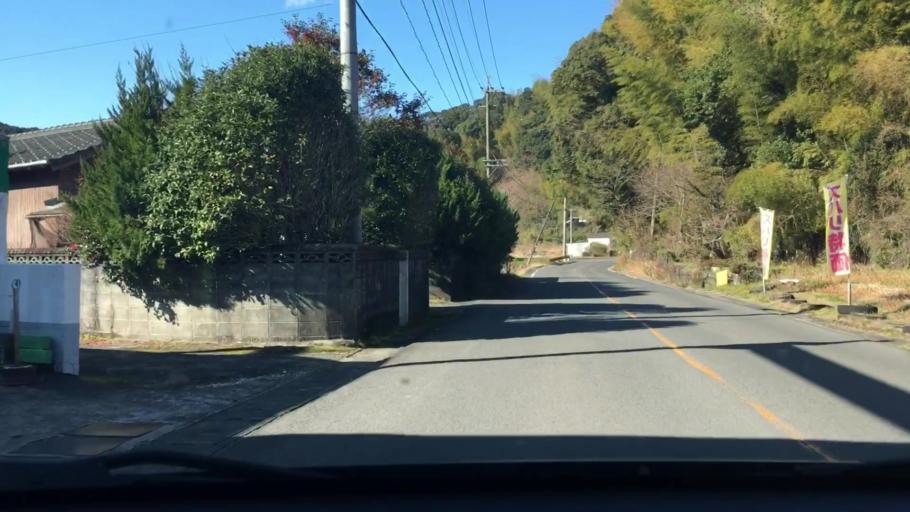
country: JP
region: Kagoshima
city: Satsumasendai
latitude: 31.7795
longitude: 130.3997
